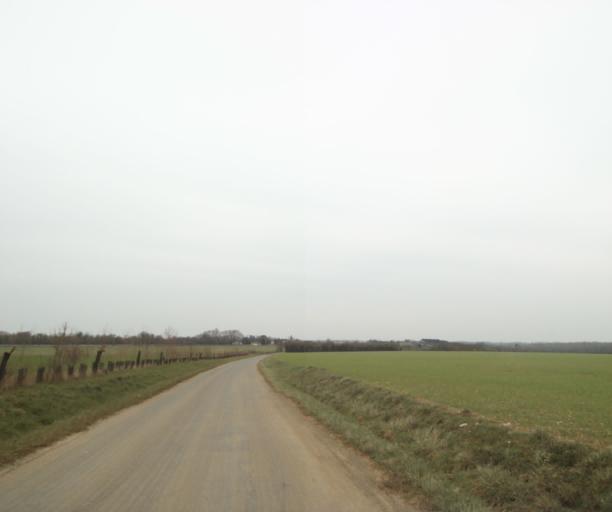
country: FR
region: Poitou-Charentes
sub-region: Departement des Deux-Sevres
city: Magne
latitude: 46.3373
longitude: -0.5208
